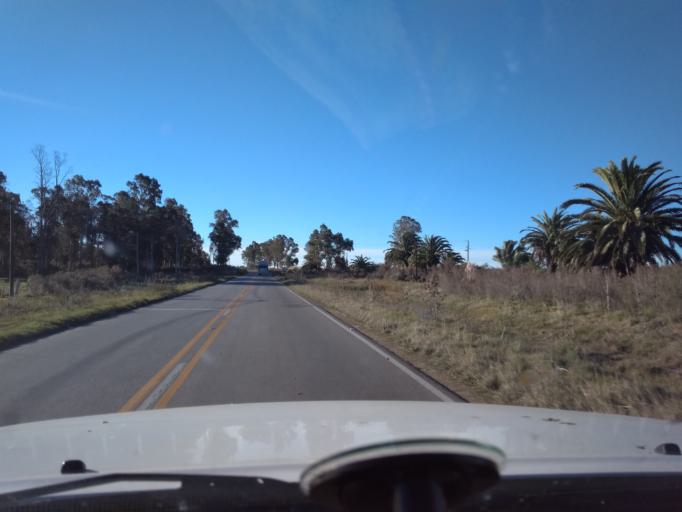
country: UY
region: Canelones
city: San Bautista
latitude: -34.4338
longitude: -55.9605
